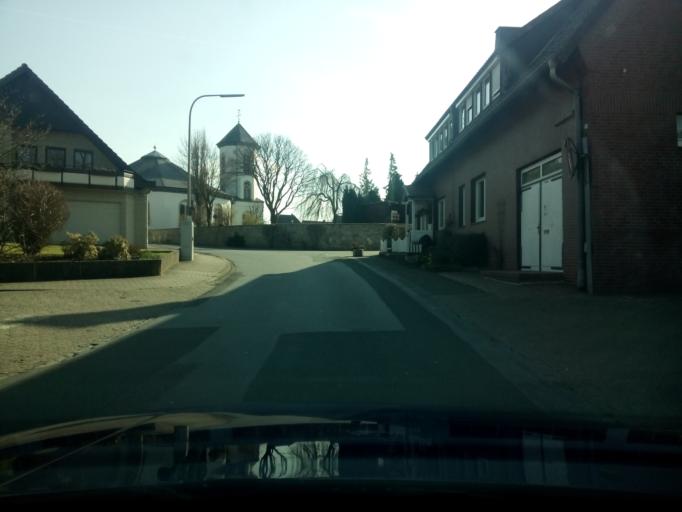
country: DE
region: Lower Saxony
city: Melle
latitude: 52.2117
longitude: 8.2730
